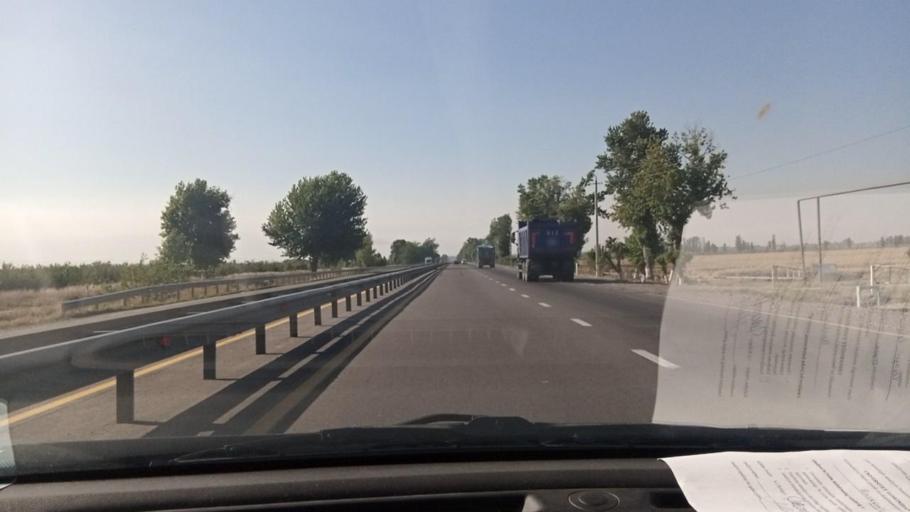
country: UZ
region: Toshkent Shahri
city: Bektemir
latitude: 41.1731
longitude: 69.4123
